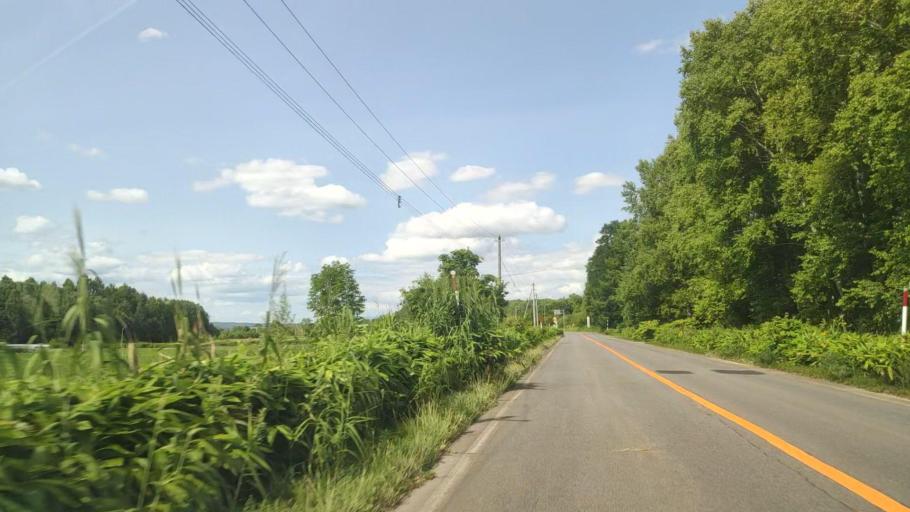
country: JP
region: Hokkaido
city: Nayoro
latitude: 44.2746
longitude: 142.4227
